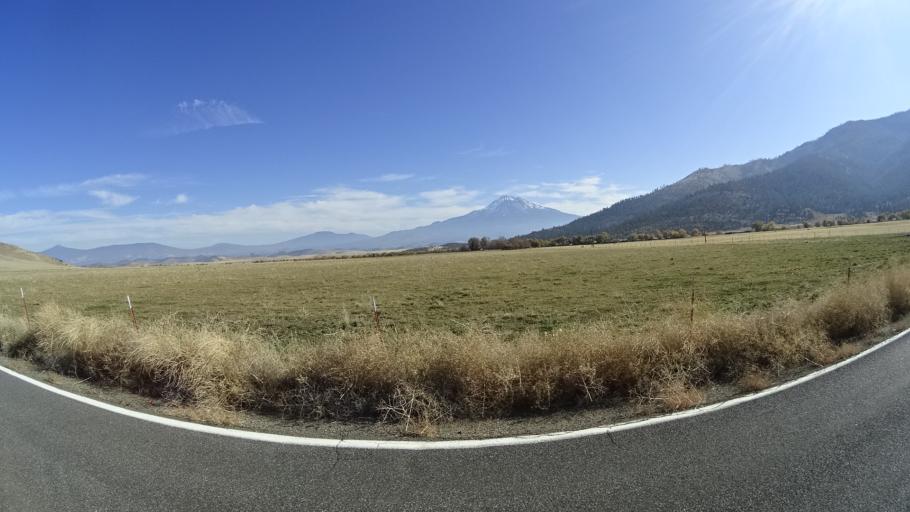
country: US
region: California
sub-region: Siskiyou County
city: Weed
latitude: 41.4982
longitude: -122.5507
